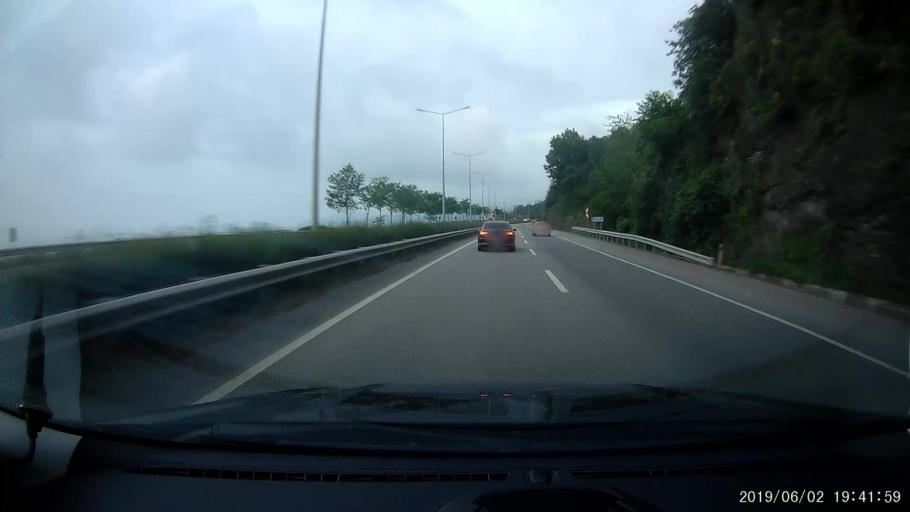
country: TR
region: Giresun
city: Kesap
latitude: 40.9156
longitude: 38.4927
